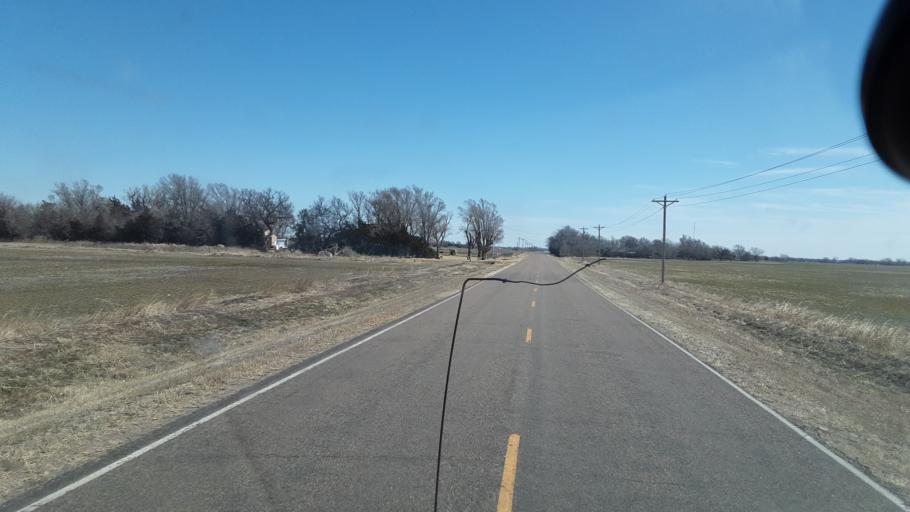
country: US
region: Kansas
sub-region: Rice County
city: Sterling
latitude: 38.2176
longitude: -98.1335
